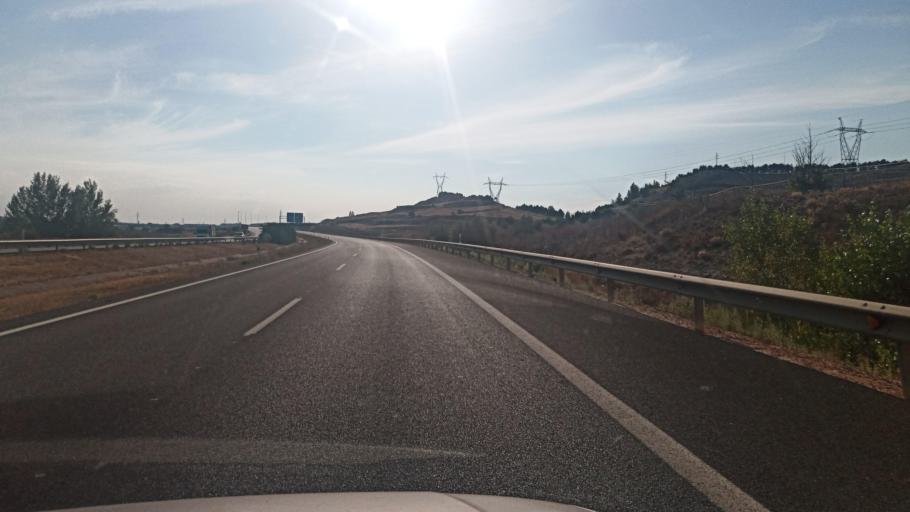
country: ES
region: Castille and Leon
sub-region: Provincia de Burgos
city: Hurones
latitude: 42.3736
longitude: -3.6172
